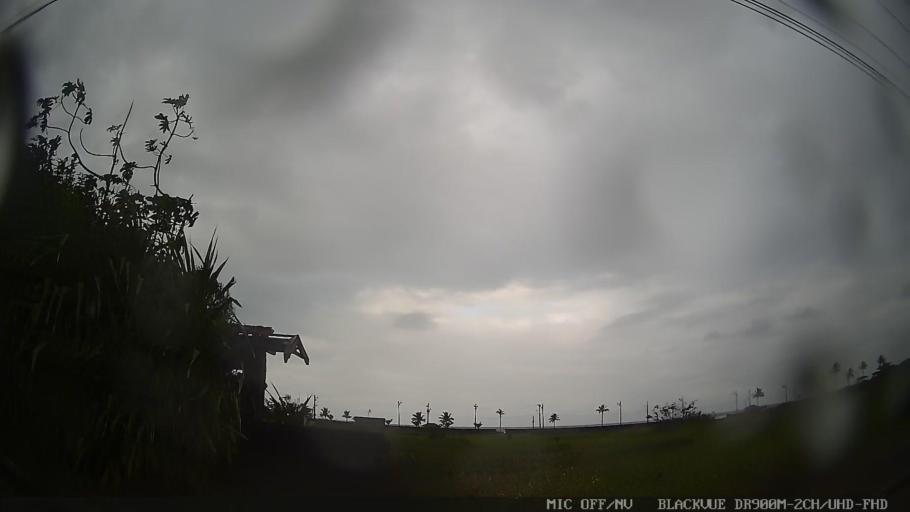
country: BR
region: Sao Paulo
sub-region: Mongagua
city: Mongagua
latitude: -24.1337
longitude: -46.6965
